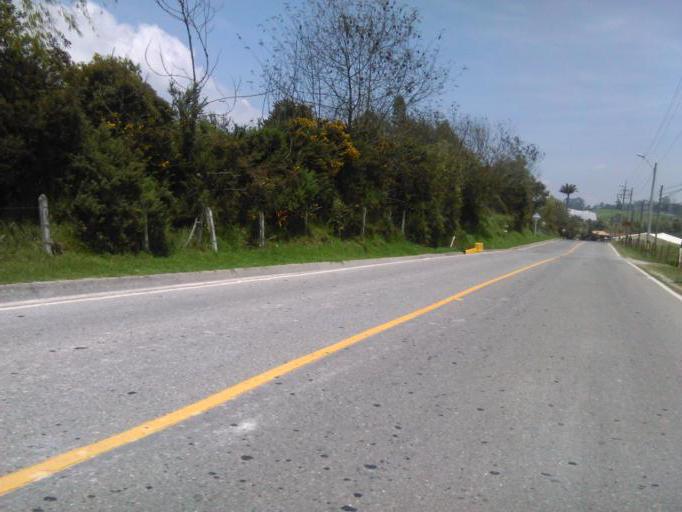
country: CO
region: Antioquia
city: La Union
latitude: 5.9873
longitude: -75.3721
